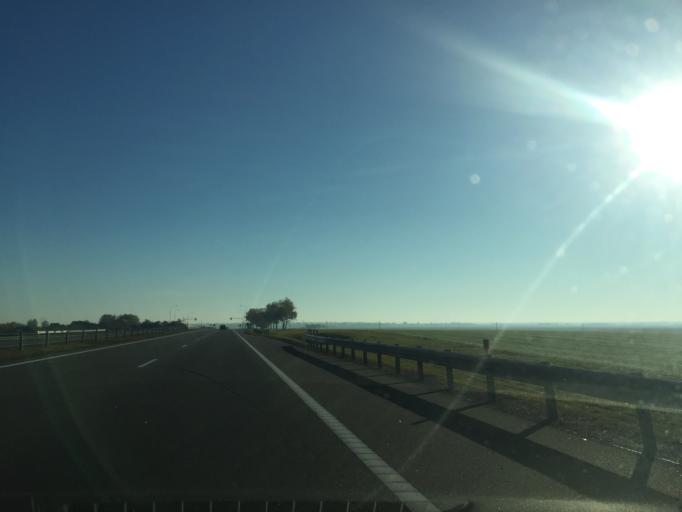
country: BY
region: Minsk
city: Zamostochcha
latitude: 53.7616
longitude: 27.9265
